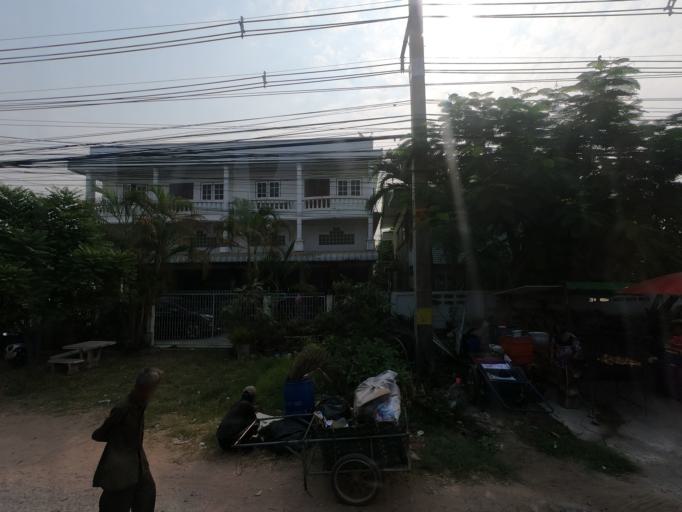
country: TH
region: Khon Kaen
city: Khon Kaen
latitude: 16.3378
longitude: 102.8012
